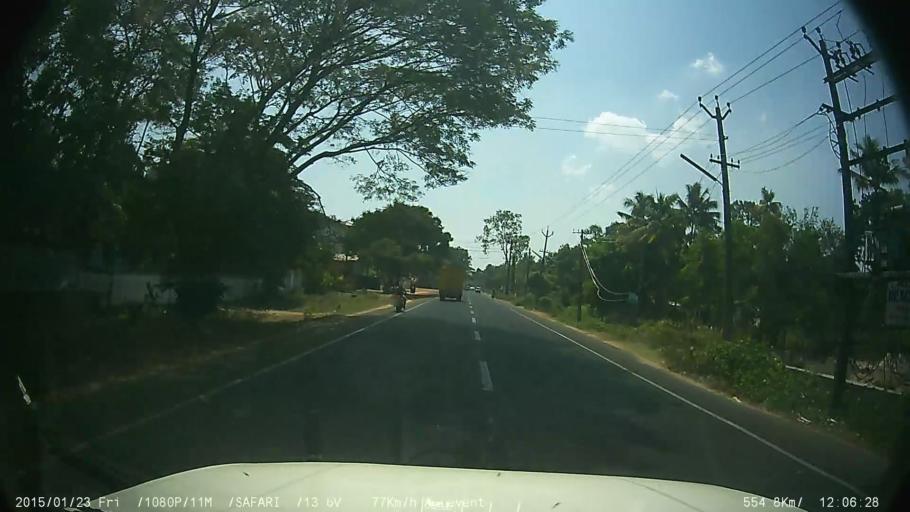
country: IN
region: Kerala
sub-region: Alappuzha
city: Shertallai
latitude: 9.5967
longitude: 76.3280
